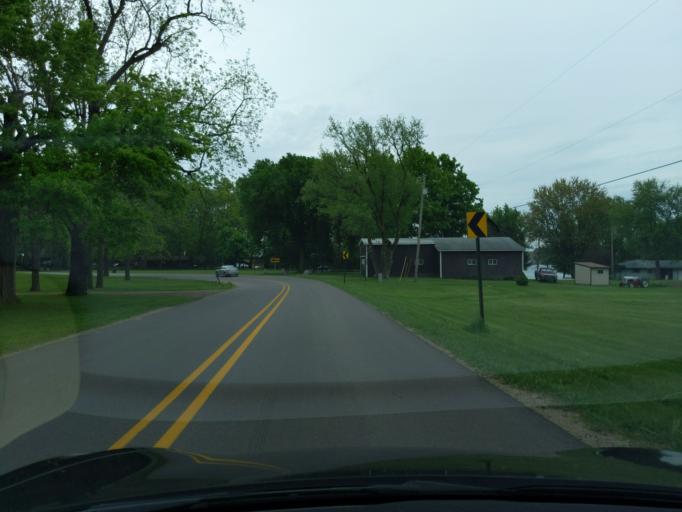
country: US
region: Michigan
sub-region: Ingham County
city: Leslie
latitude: 42.3869
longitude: -84.3493
